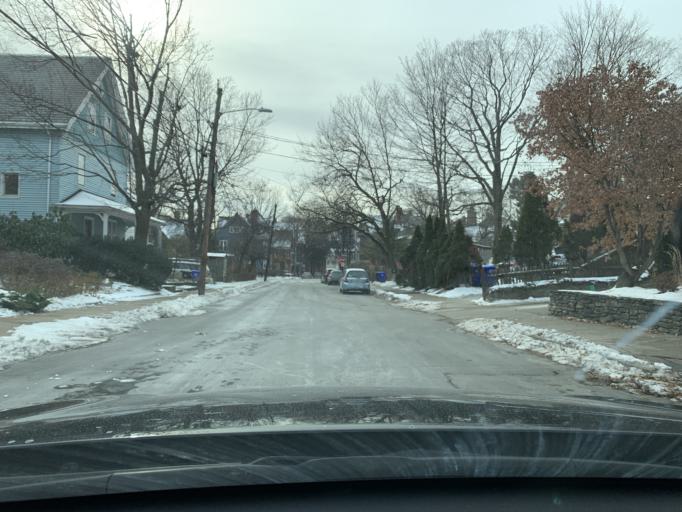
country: US
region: Massachusetts
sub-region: Norfolk County
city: Brookline
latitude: 42.3378
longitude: -71.1171
